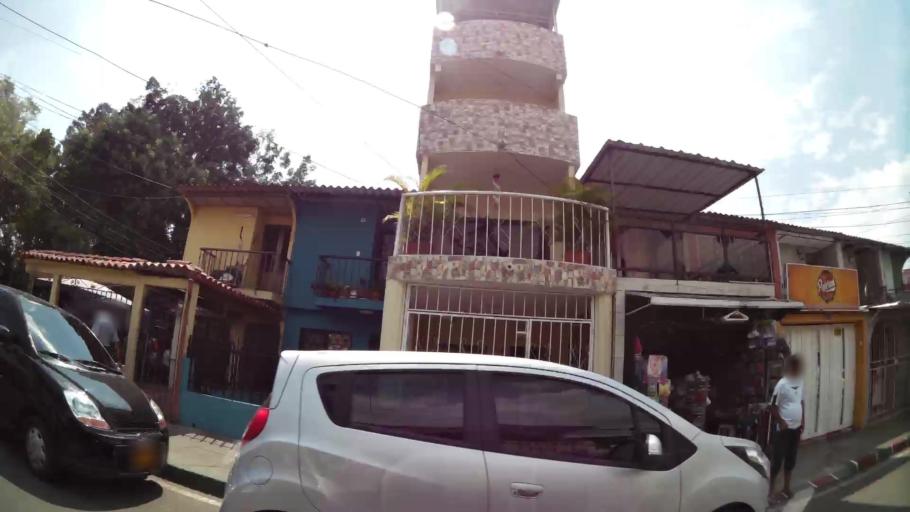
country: CO
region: Valle del Cauca
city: Cali
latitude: 3.4935
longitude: -76.5027
